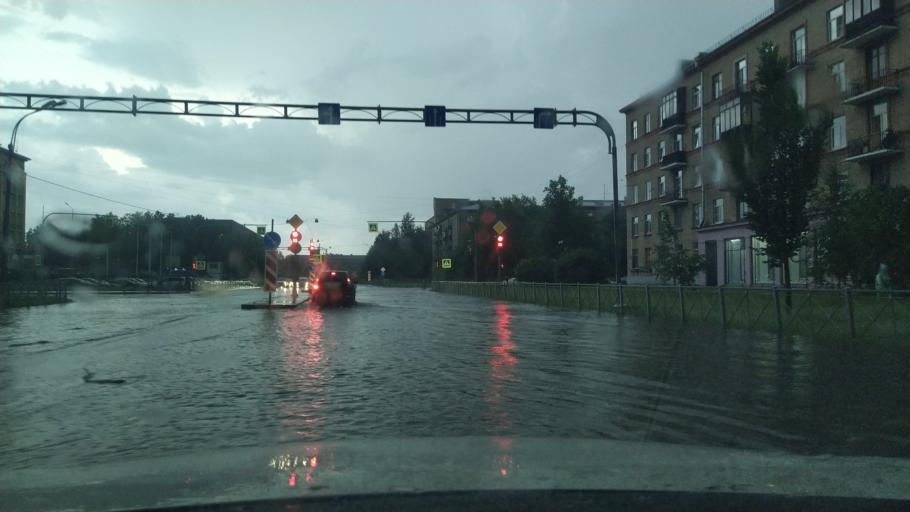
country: RU
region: Leningrad
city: Sampsonievskiy
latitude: 59.9818
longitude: 30.3537
